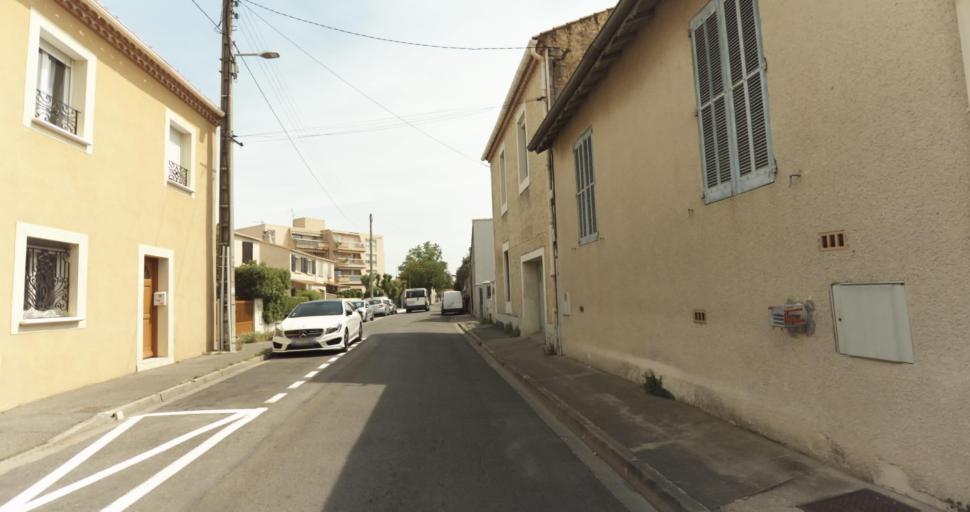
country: FR
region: Languedoc-Roussillon
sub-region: Departement du Gard
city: Nimes
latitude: 43.8285
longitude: 4.3675
